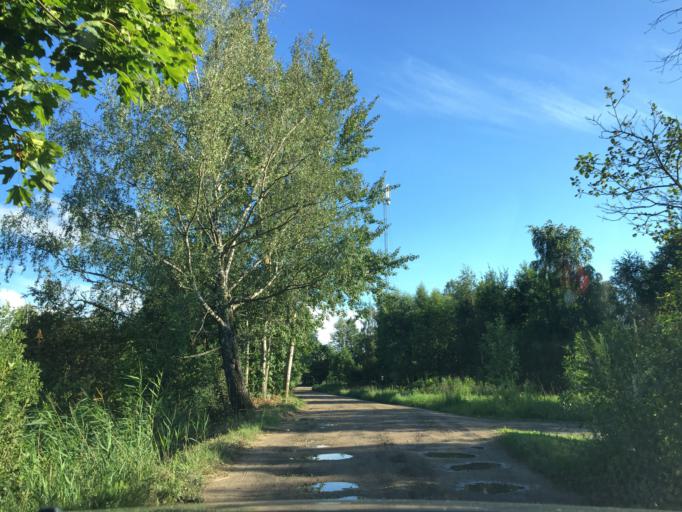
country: LV
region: Riga
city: Jaunciems
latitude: 57.0542
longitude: 24.1317
